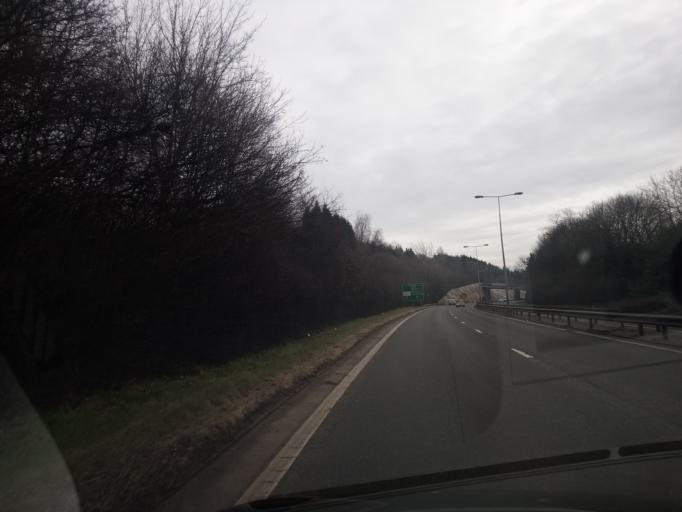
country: GB
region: England
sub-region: Telford and Wrekin
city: Oakengates
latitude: 52.7011
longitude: -2.4531
